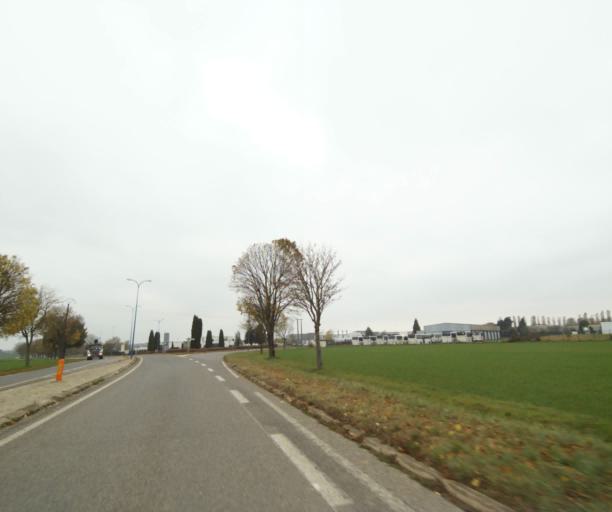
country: FR
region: Lorraine
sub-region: Departement de Meurthe-et-Moselle
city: Moutiers
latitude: 49.2503
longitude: 5.9702
